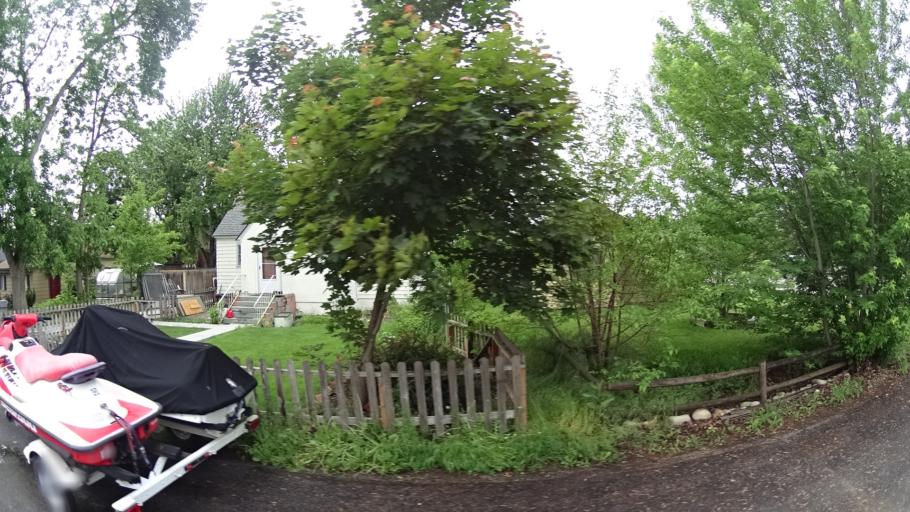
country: US
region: Idaho
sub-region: Ada County
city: Eagle
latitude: 43.6962
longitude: -116.3525
